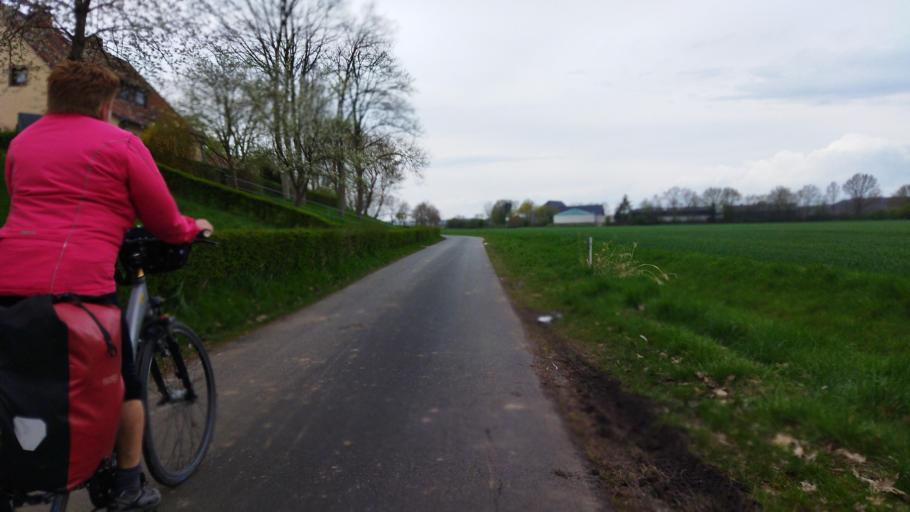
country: DE
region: Lower Saxony
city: Ahsen-Oetzen
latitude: 52.9841
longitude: 9.1206
